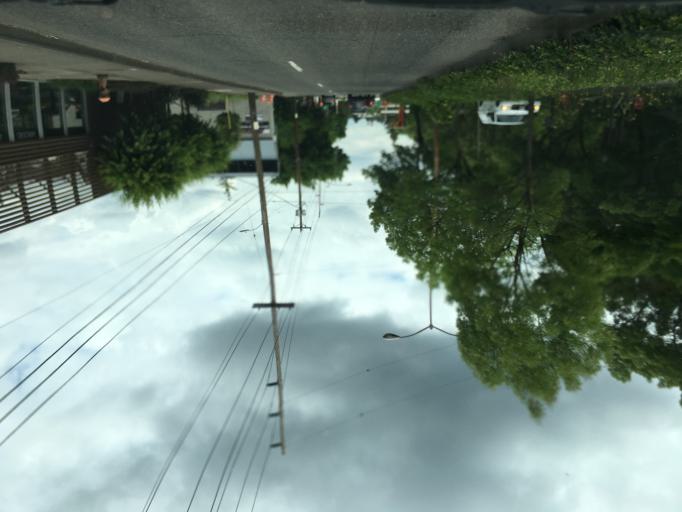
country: US
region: Oregon
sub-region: Clackamas County
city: Milwaukie
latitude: 45.4693
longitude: -122.6714
